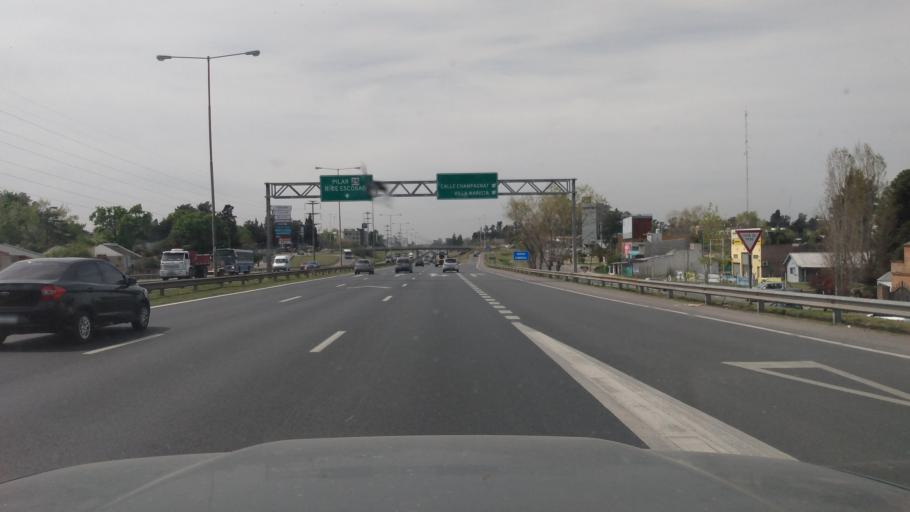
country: AR
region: Buenos Aires
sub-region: Partido de Pilar
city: Pilar
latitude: -34.4518
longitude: -58.9210
